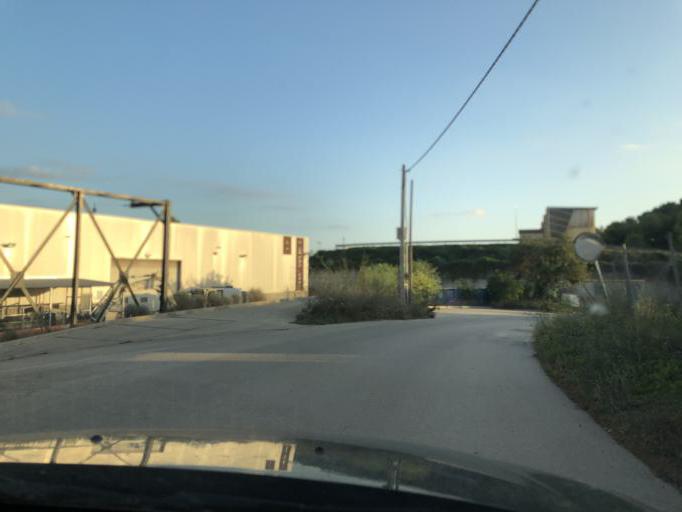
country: ES
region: Balearic Islands
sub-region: Illes Balears
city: Santa Ponsa
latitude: 39.5392
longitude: 2.4841
